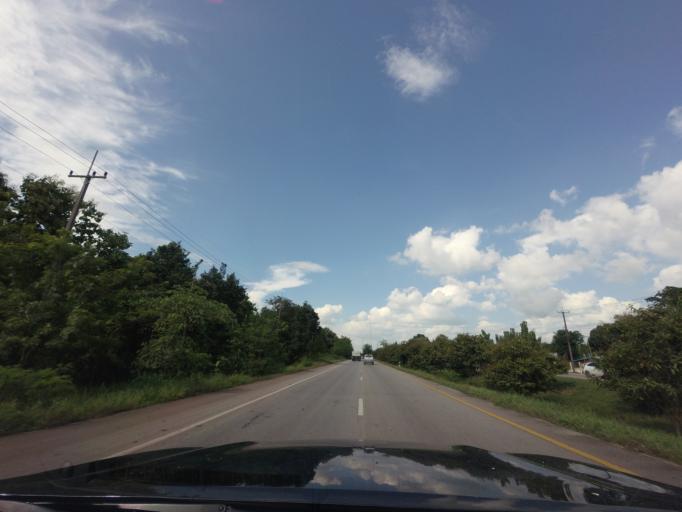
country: TH
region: Nong Khai
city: Sa Khrai
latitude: 17.6547
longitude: 102.7891
